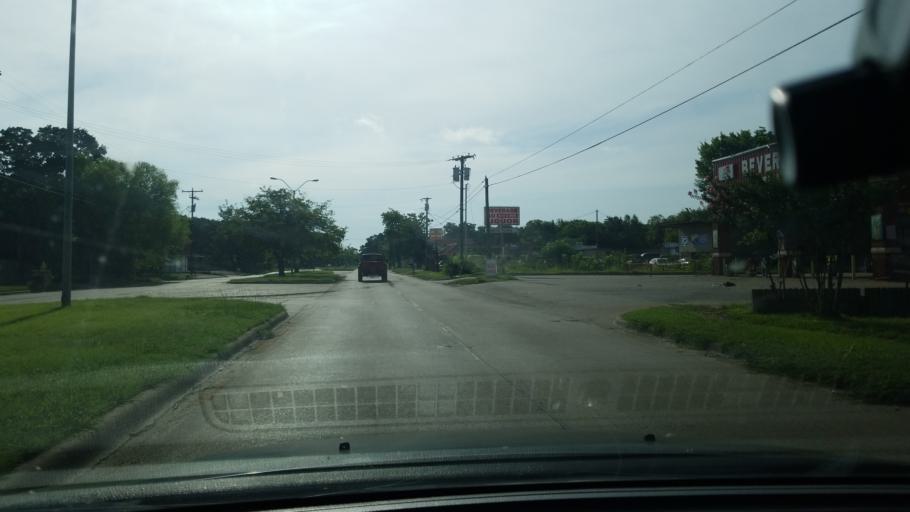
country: US
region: Texas
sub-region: Dallas County
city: Balch Springs
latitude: 32.7194
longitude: -96.6379
